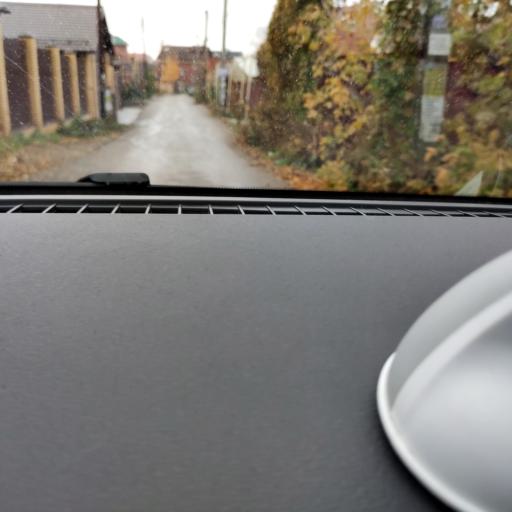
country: RU
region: Samara
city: Samara
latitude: 53.2698
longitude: 50.2073
